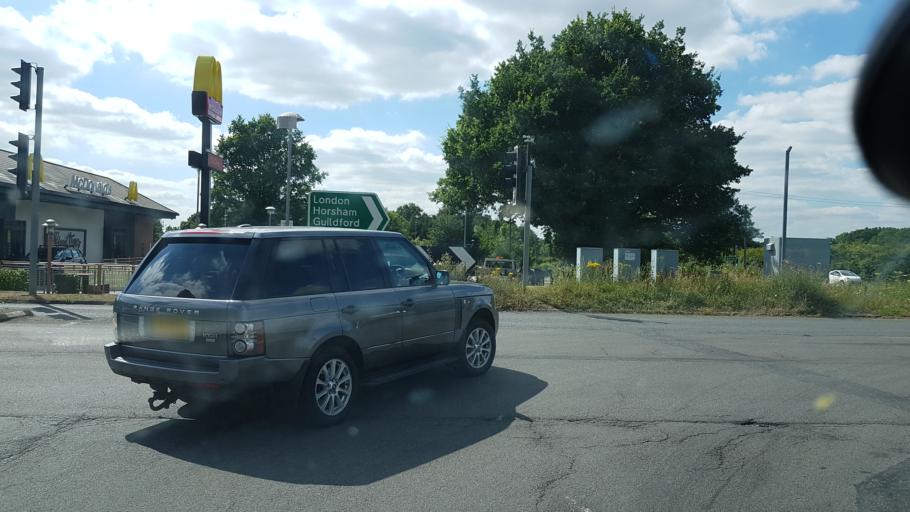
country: GB
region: England
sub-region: West Sussex
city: Southwater
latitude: 50.9919
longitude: -0.3404
